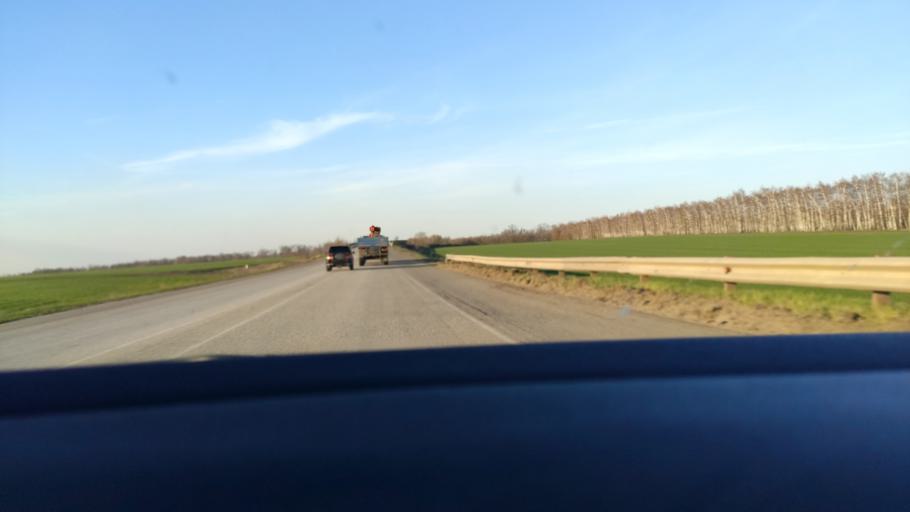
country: RU
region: Voronezj
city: Kolodeznyy
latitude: 51.4035
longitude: 39.2407
